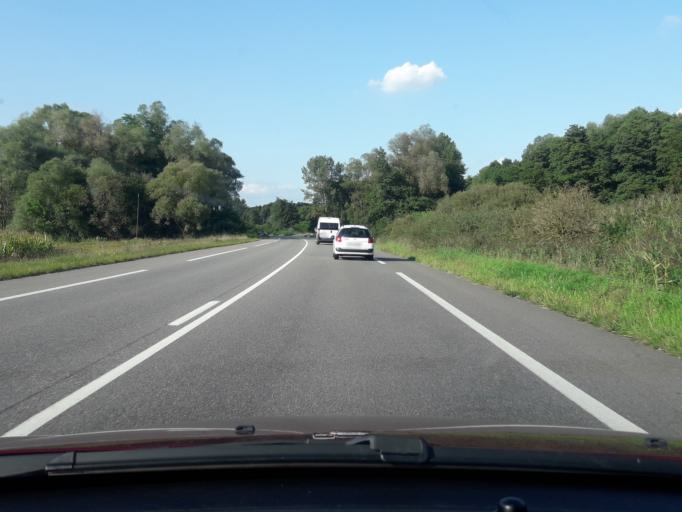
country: FR
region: Alsace
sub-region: Departement du Bas-Rhin
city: Wissembourg
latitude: 48.9802
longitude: 7.9575
